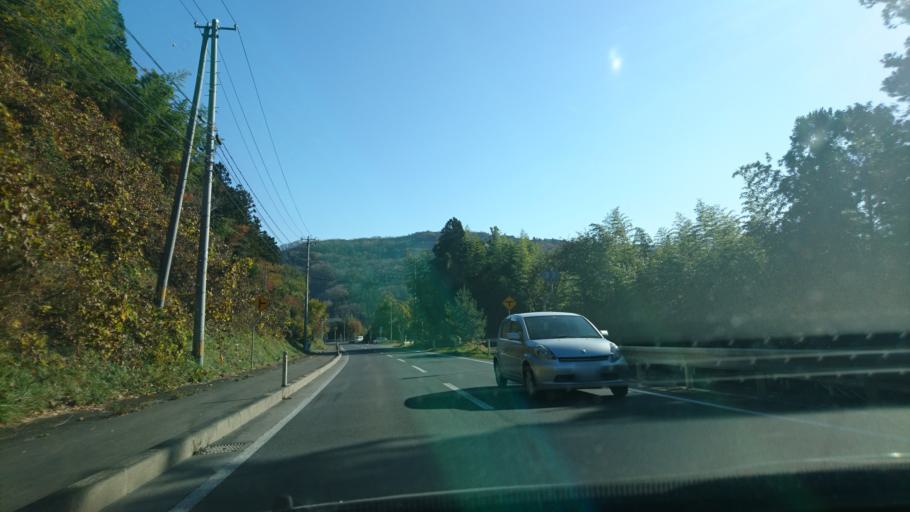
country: JP
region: Iwate
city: Ichinoseki
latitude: 38.9810
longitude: 141.2368
